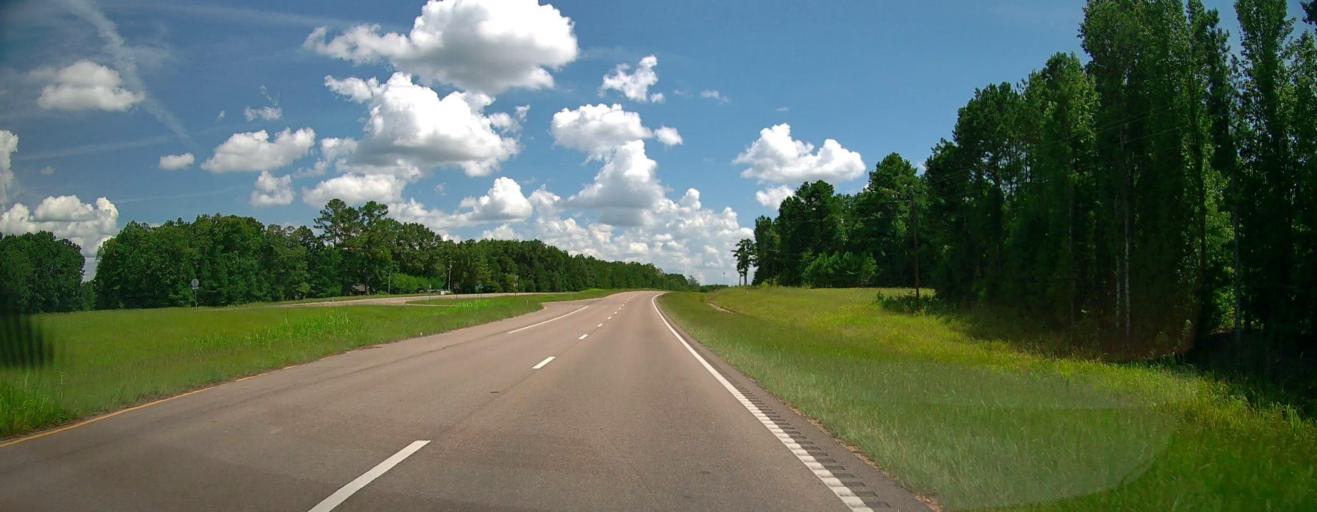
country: US
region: Mississippi
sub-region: Monroe County
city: Amory
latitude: 33.9414
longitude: -88.5988
